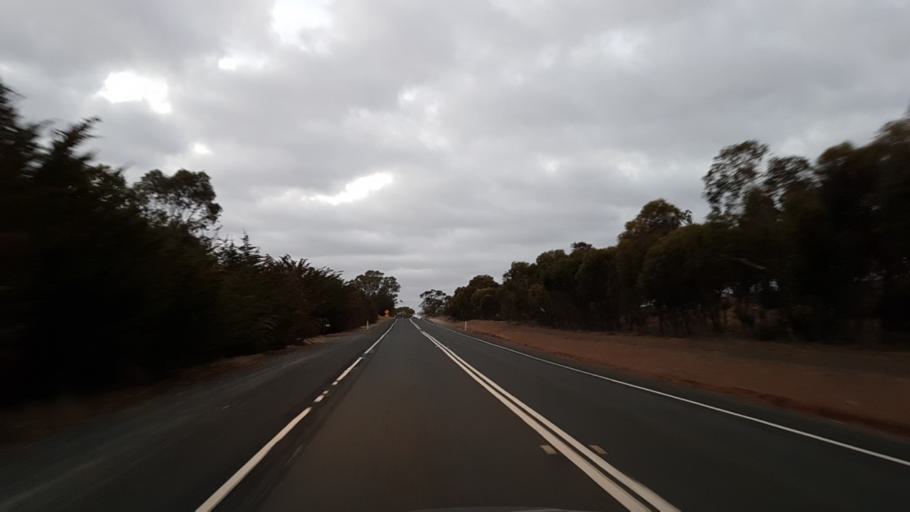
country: AU
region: South Australia
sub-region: Mount Barker
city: Nairne
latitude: -35.0454
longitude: 138.9967
